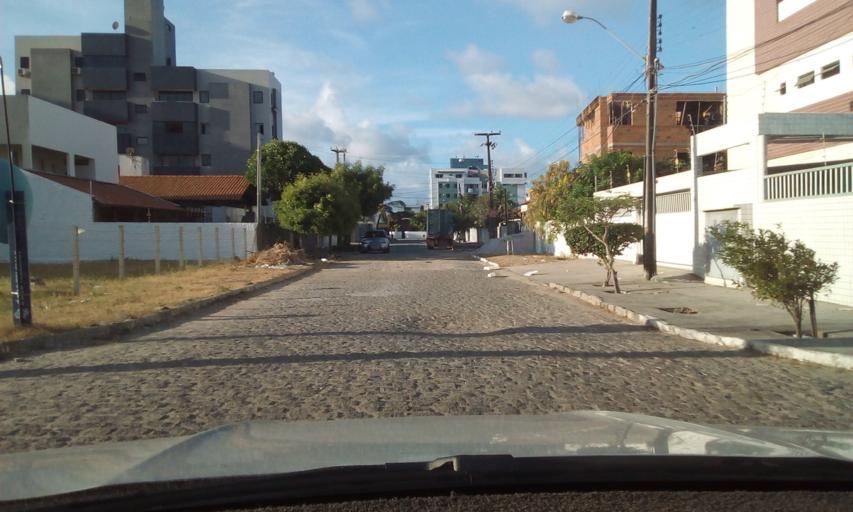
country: BR
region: Paraiba
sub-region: Joao Pessoa
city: Joao Pessoa
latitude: -7.0642
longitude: -34.8425
